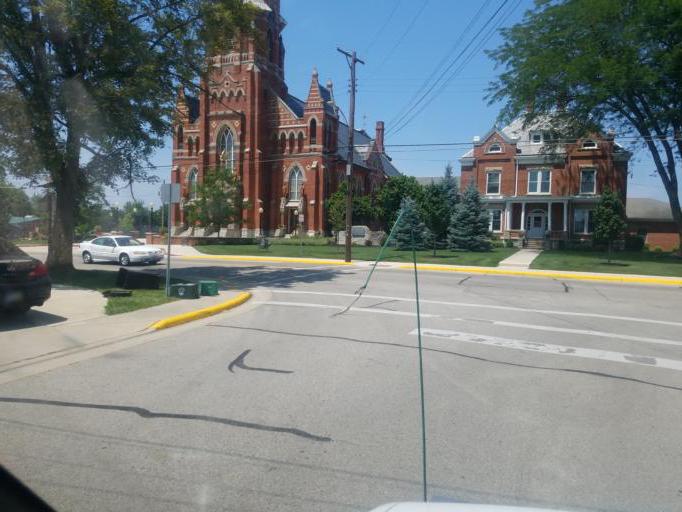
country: US
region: Ohio
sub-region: Shelby County
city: Fort Loramie
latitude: 40.3506
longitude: -84.3713
